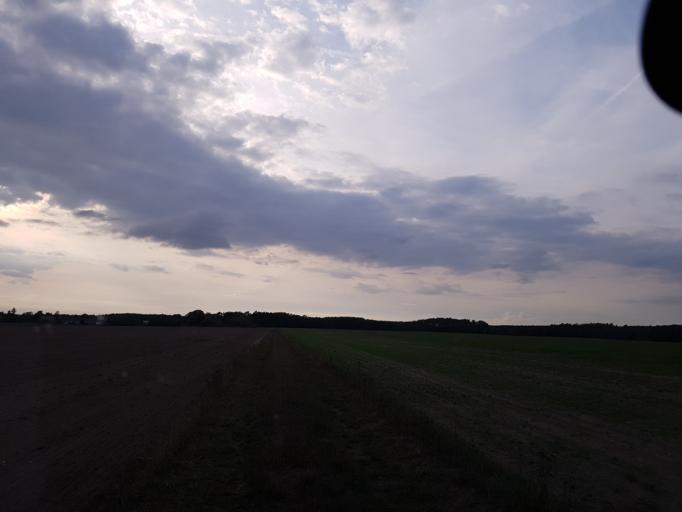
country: DE
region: Brandenburg
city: Bad Liebenwerda
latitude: 51.5507
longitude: 13.3957
